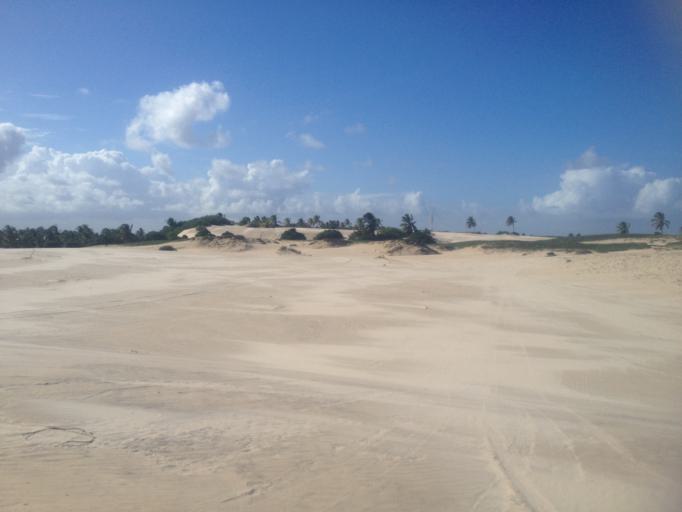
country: BR
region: Sergipe
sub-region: Indiaroba
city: Indiaroba
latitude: -11.4706
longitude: -37.3694
